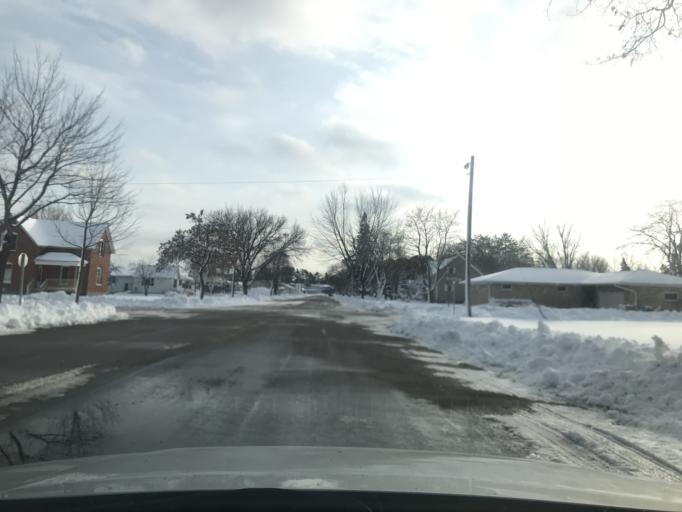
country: US
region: Wisconsin
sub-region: Marinette County
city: Peshtigo
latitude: 45.0487
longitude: -87.7548
